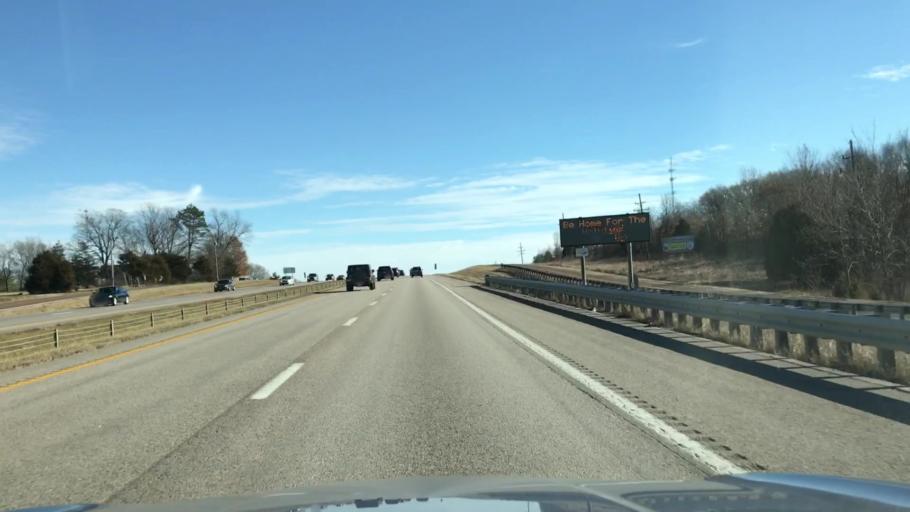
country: US
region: Missouri
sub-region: Warren County
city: Warrenton
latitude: 38.8233
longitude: -91.1961
